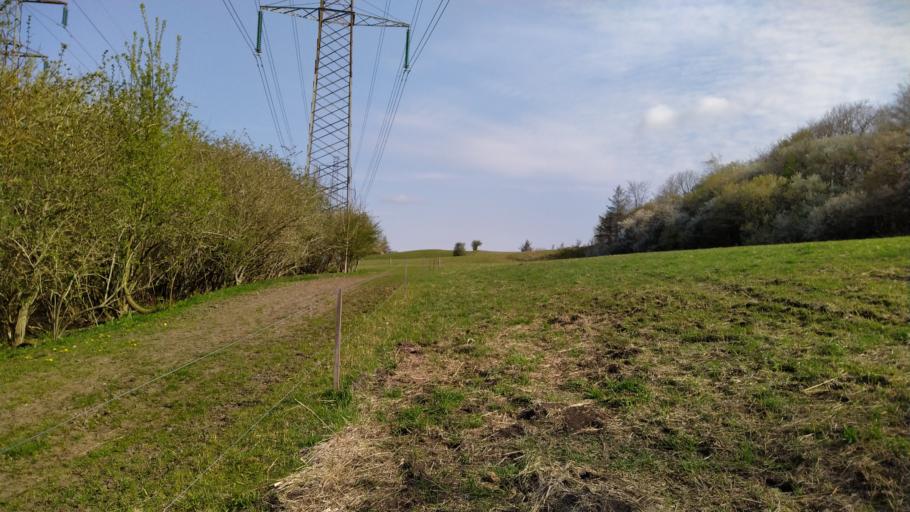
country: DK
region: Capital Region
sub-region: Egedal Kommune
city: Stenlose
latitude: 55.7517
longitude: 12.2136
